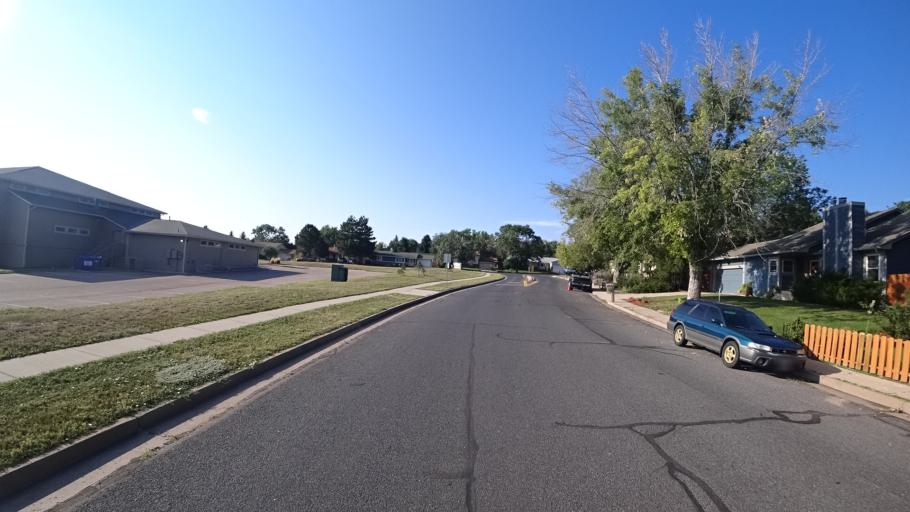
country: US
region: Colorado
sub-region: El Paso County
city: Colorado Springs
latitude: 38.8892
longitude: -104.8444
